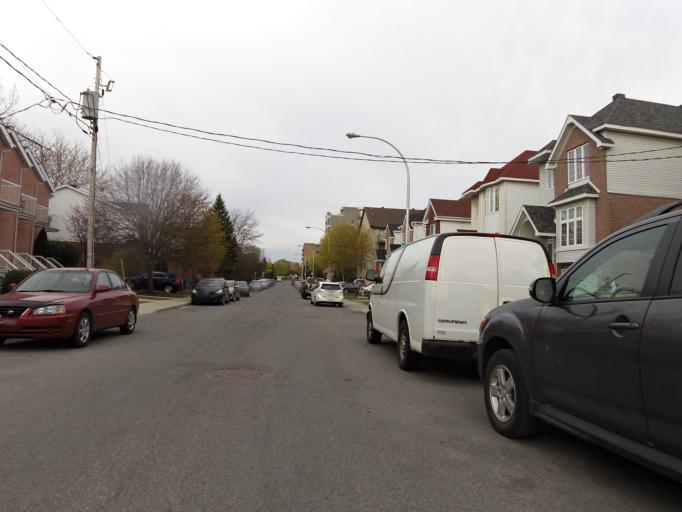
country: CA
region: Quebec
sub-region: Laval
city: Laval
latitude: 45.5328
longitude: -73.7411
